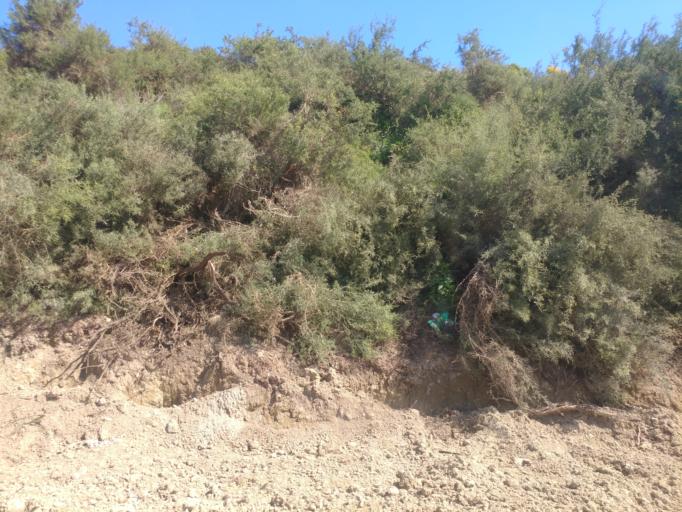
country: CY
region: Pafos
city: Polis
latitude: 34.9920
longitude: 32.4499
